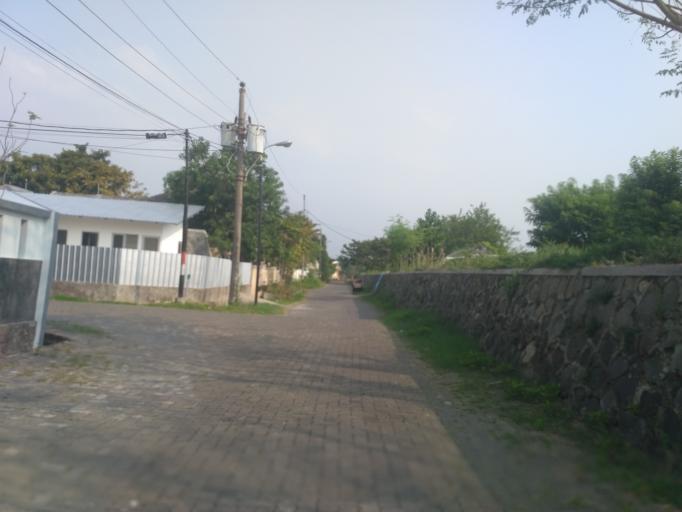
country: ID
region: Central Java
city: Semarang
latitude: -6.9662
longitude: 110.3841
